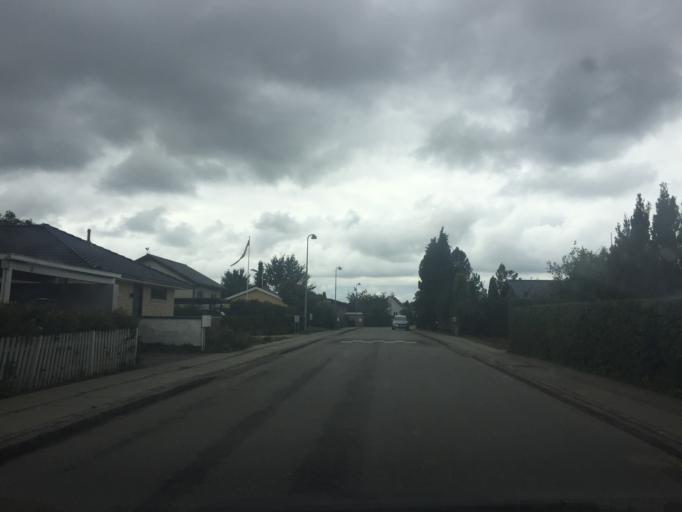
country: DK
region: Capital Region
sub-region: Gladsaxe Municipality
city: Buddinge
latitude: 55.7616
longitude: 12.4771
